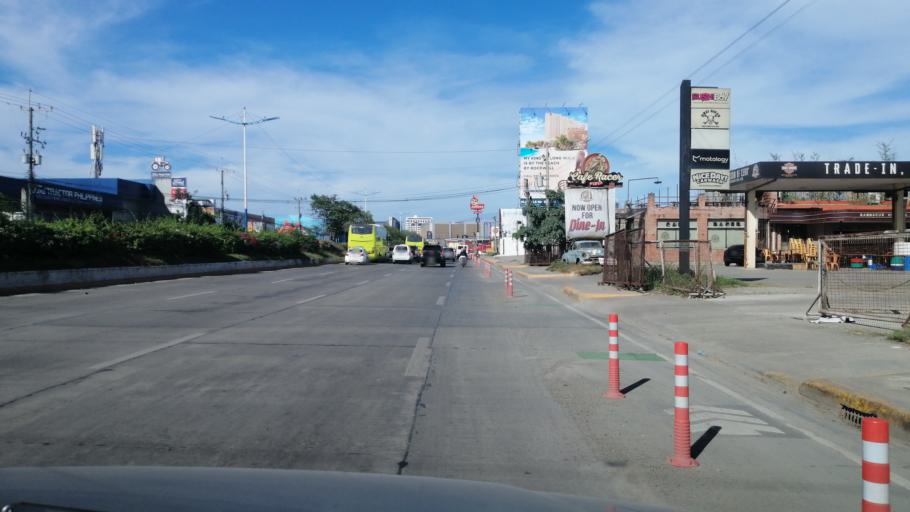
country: PH
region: Central Visayas
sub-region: Cebu City
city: Baugo
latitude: 10.3153
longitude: 123.9274
